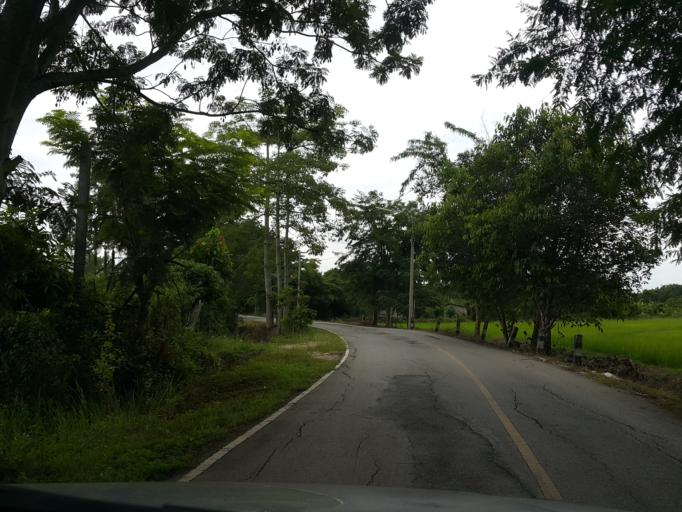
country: TH
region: Chiang Mai
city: San Kamphaeng
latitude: 18.8069
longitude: 99.1416
